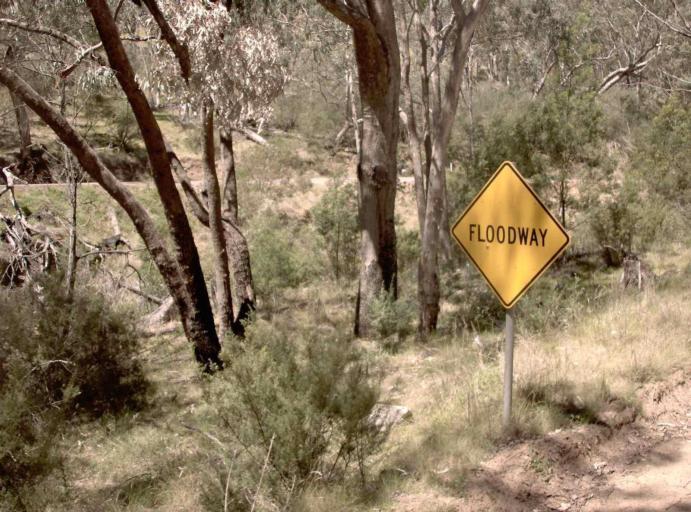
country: AU
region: New South Wales
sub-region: Snowy River
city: Jindabyne
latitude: -37.0763
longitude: 148.4937
